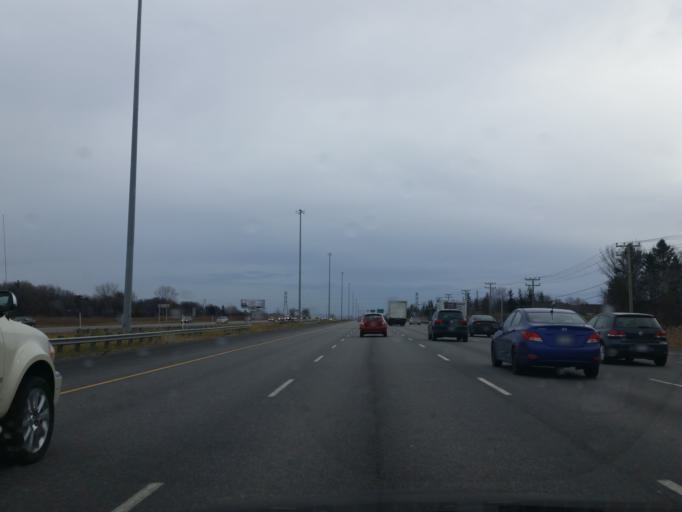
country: CA
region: Quebec
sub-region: Laurentides
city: Blainville
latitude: 45.6519
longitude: -73.8765
